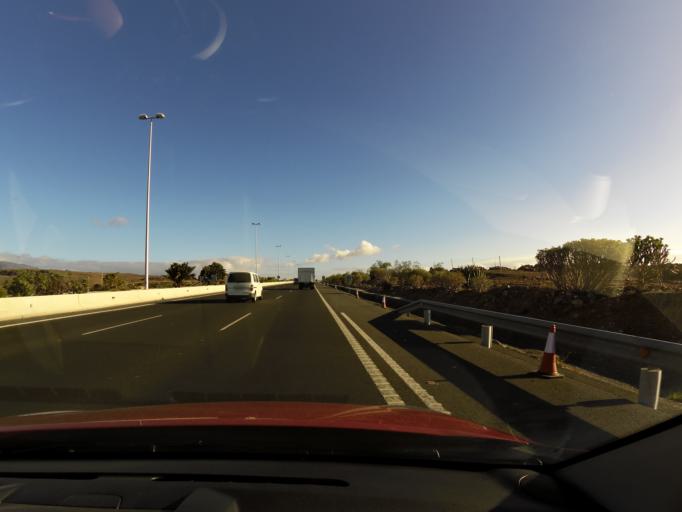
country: ES
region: Canary Islands
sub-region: Provincia de Las Palmas
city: Cruce de Arinaga
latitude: 27.8075
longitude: -15.4801
